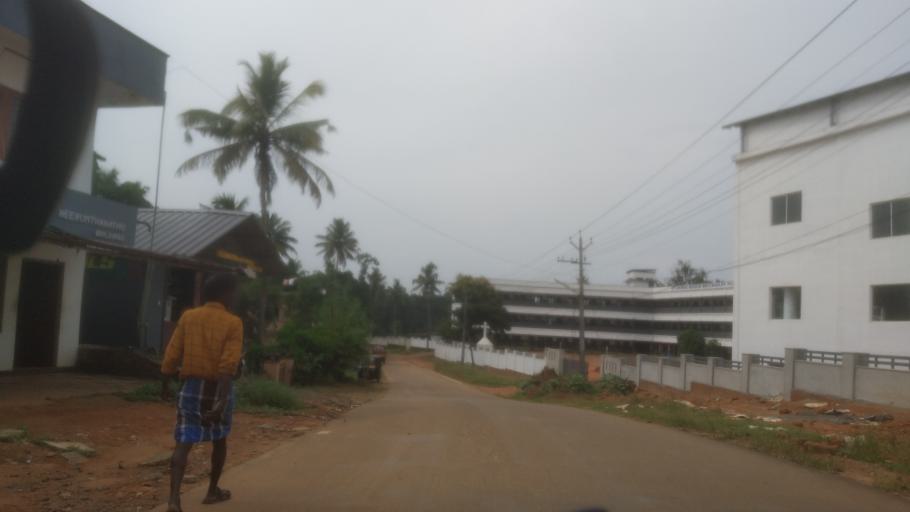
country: IN
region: Kerala
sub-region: Ernakulam
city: Muvattupula
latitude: 10.0471
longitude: 76.5312
